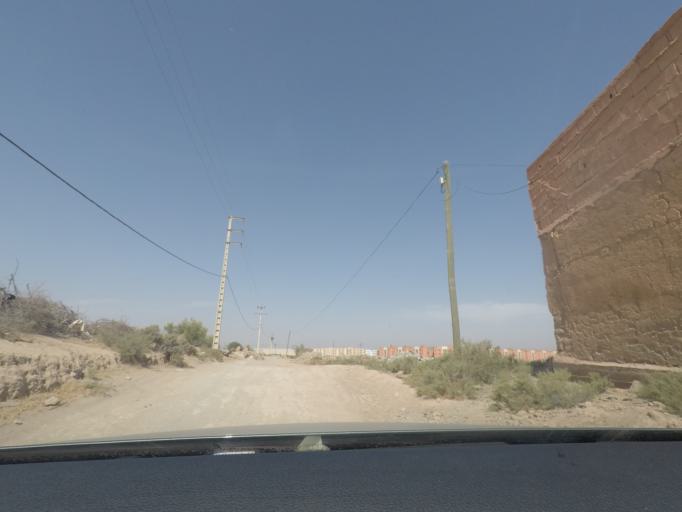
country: MA
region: Marrakech-Tensift-Al Haouz
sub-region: Marrakech
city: Marrakesh
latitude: 31.5827
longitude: -8.0271
